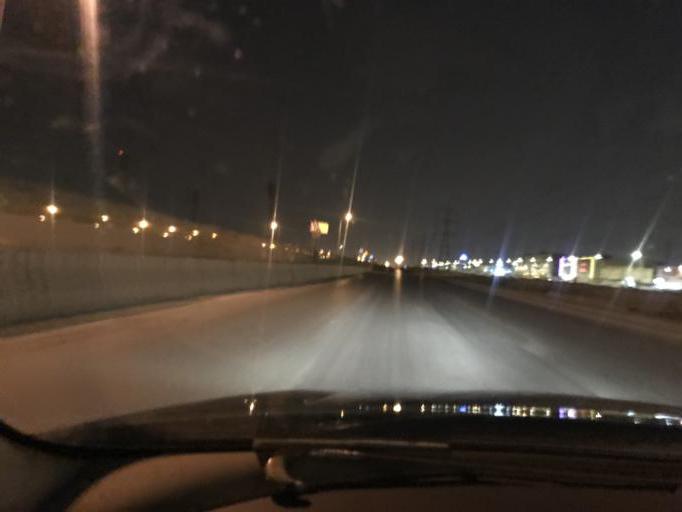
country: SA
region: Ar Riyad
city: Riyadh
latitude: 24.8029
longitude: 46.7003
